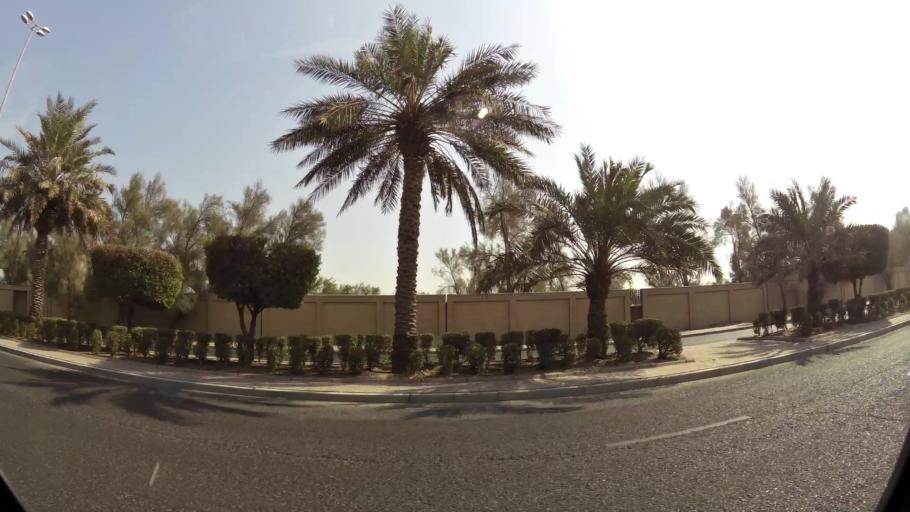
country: KW
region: Al Ahmadi
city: Al Fintas
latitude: 29.1626
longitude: 48.1221
